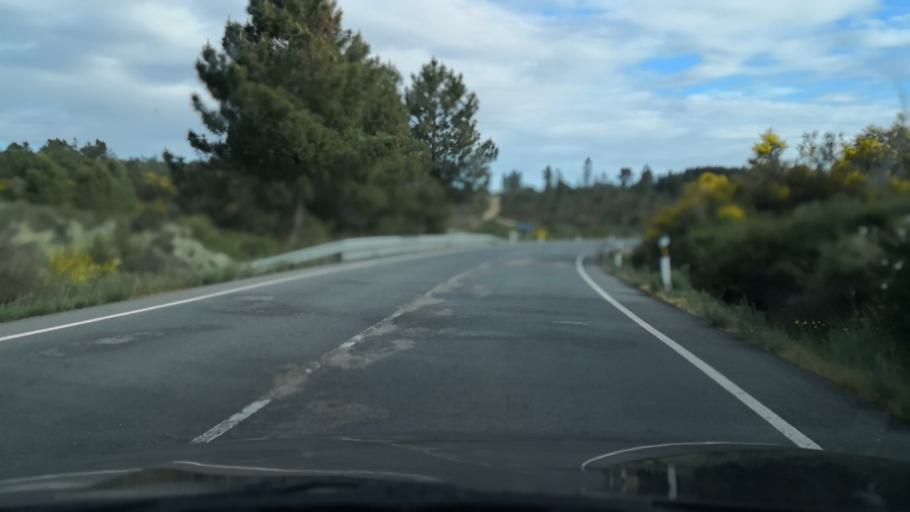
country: ES
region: Extremadura
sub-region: Provincia de Caceres
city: Perales del Puerto
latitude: 40.1444
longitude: -6.6762
